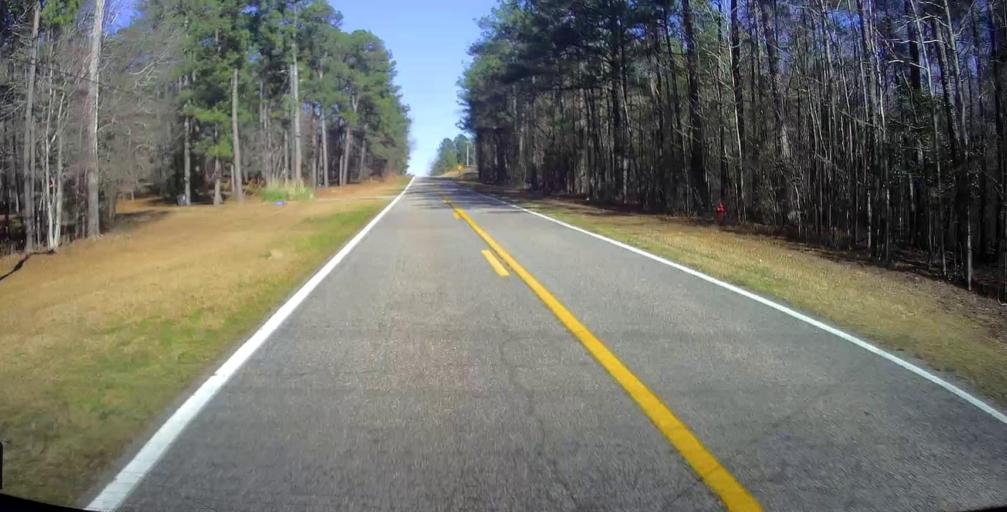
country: US
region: Georgia
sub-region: Peach County
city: Fort Valley
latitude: 32.6498
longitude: -83.8880
